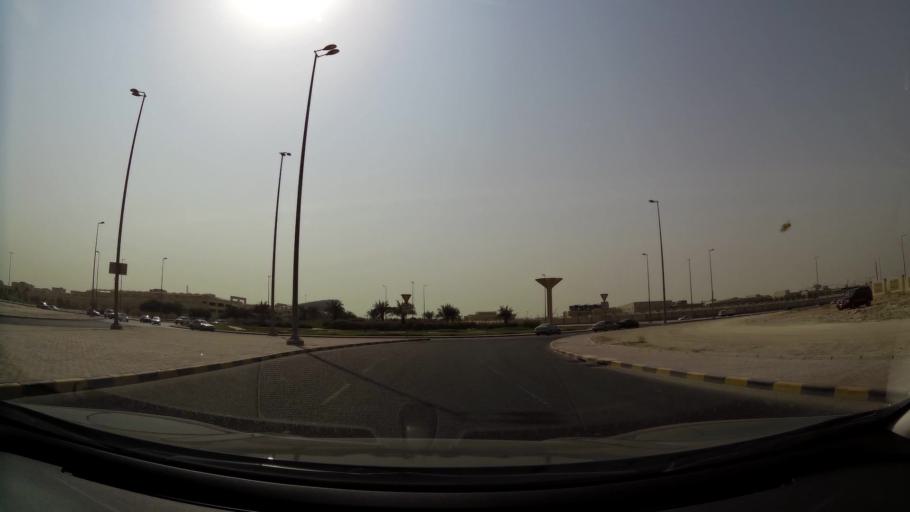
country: KW
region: Al Asimah
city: Ar Rabiyah
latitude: 29.2800
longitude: 47.9146
